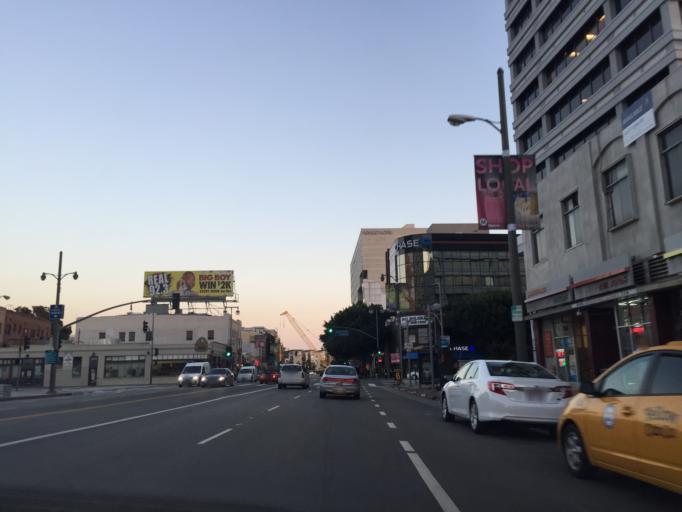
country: US
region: California
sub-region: Los Angeles County
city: Los Angeles
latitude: 34.0507
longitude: -118.2415
